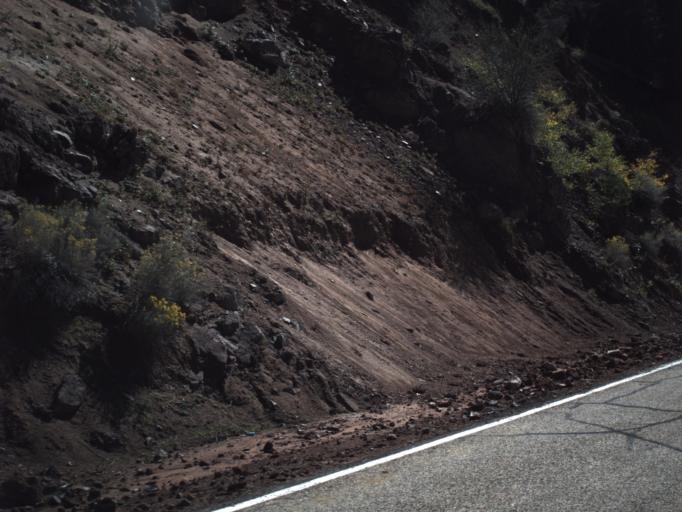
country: US
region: Utah
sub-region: Beaver County
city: Beaver
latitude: 38.2687
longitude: -112.4803
